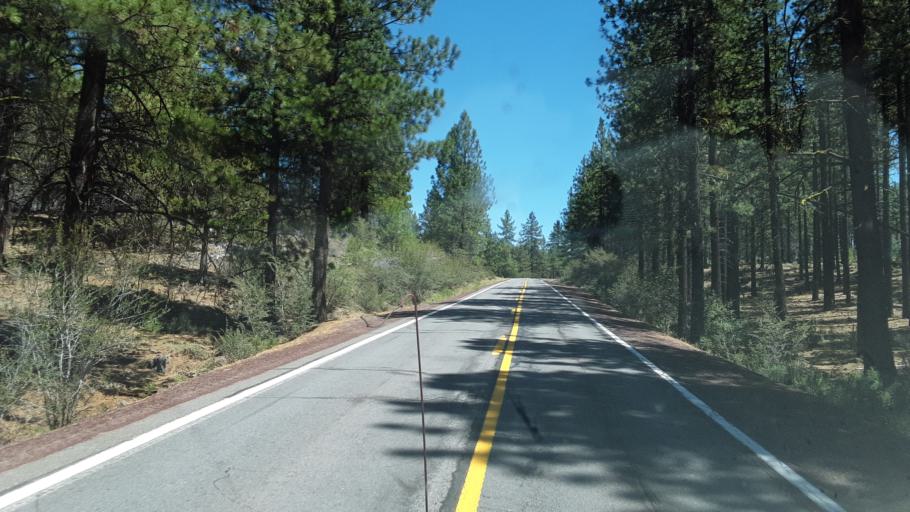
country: US
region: California
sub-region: Lassen County
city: Johnstonville
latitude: 40.4885
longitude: -120.5519
